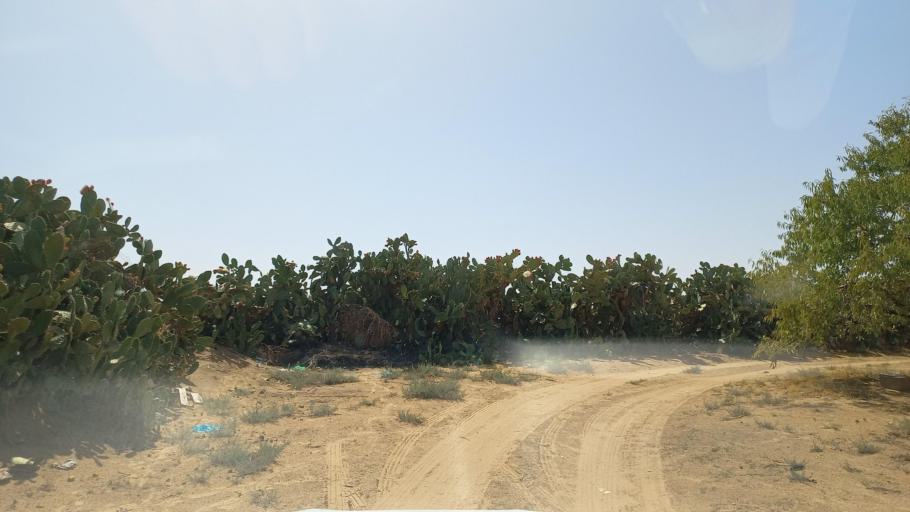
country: TN
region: Al Qasrayn
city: Kasserine
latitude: 35.2347
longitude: 9.0277
